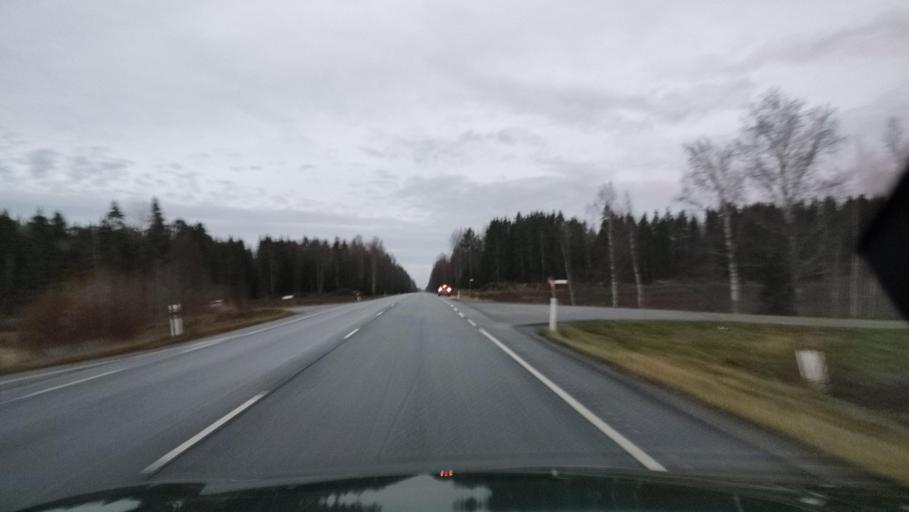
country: FI
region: Ostrobothnia
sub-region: Vaasa
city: Ristinummi
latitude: 63.0066
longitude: 21.7629
